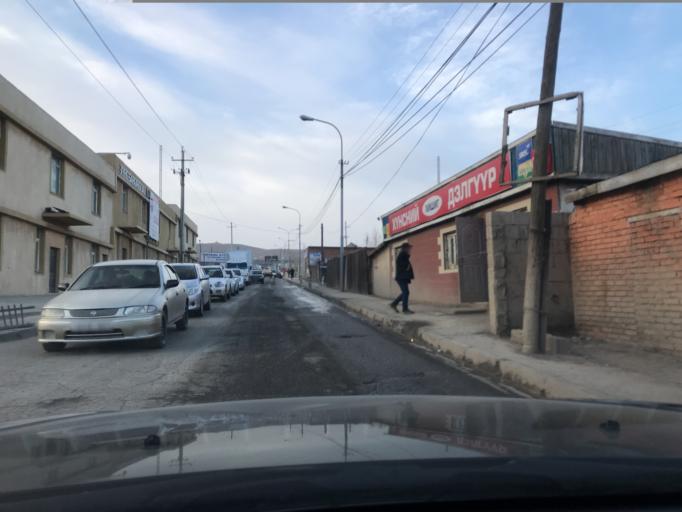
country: MN
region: Ulaanbaatar
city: Ulaanbaatar
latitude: 47.9277
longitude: 106.9981
